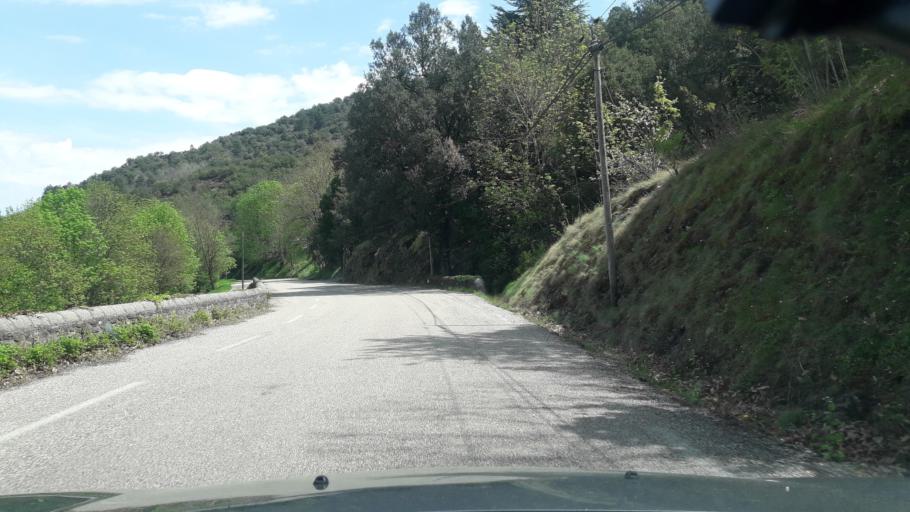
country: FR
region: Languedoc-Roussillon
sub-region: Departement du Gard
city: Valleraugue
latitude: 44.1176
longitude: 3.7264
